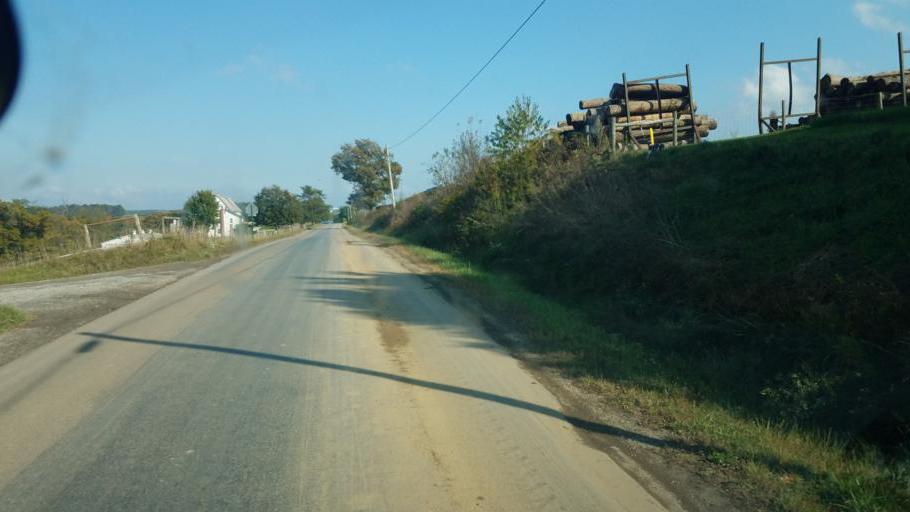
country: US
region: Ohio
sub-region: Wayne County
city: Apple Creek
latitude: 40.6749
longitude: -81.8454
